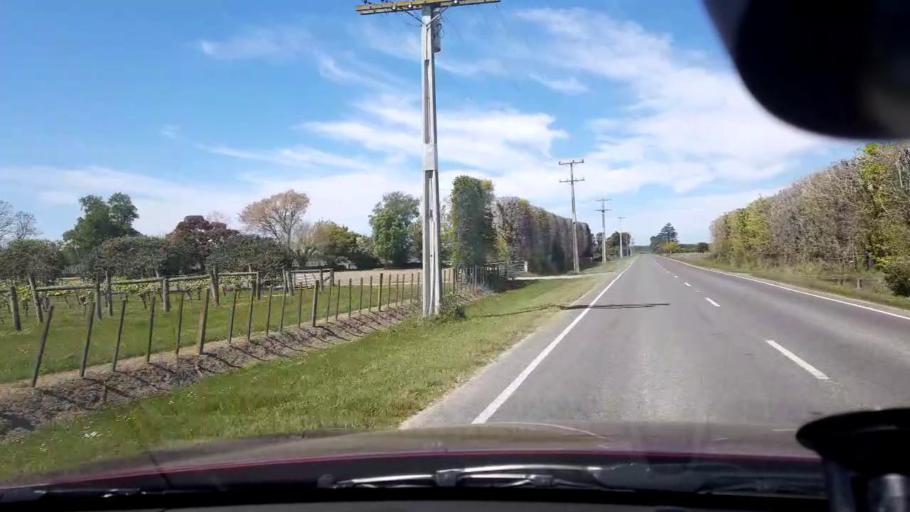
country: NZ
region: Gisborne
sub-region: Gisborne District
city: Gisborne
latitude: -38.6336
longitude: 177.9289
